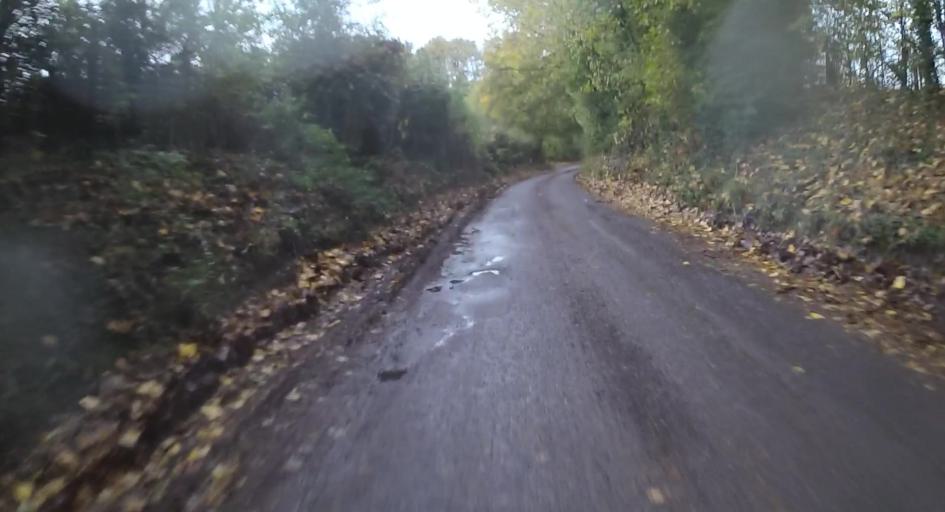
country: GB
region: England
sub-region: Hampshire
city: Kingsley
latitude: 51.1740
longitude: -0.8982
